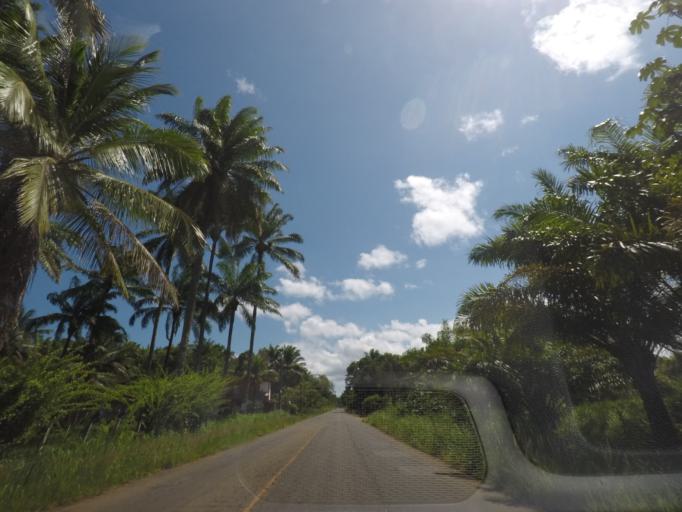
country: BR
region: Bahia
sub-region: Taperoa
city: Taperoa
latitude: -13.4865
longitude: -39.0918
